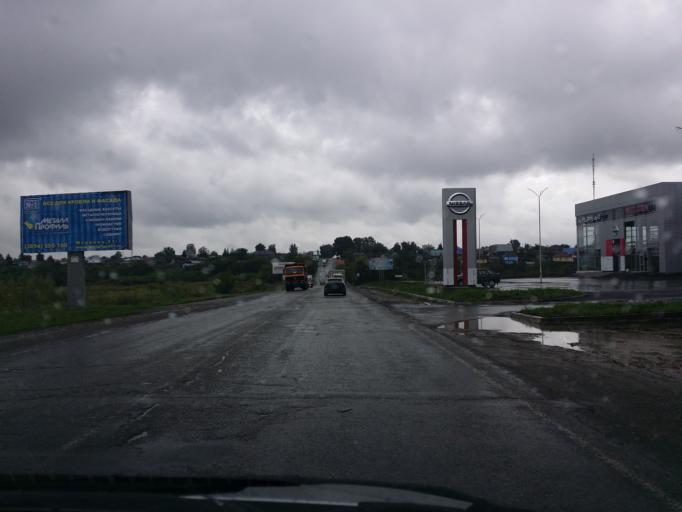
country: RU
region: Altai Krai
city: Biysk
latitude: 52.5593
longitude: 85.1944
